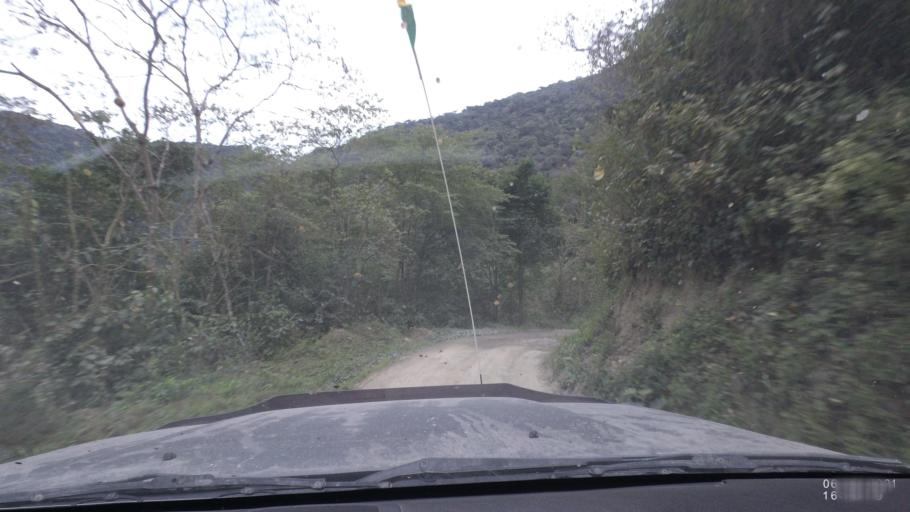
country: BO
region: La Paz
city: Quime
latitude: -16.5270
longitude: -66.7529
